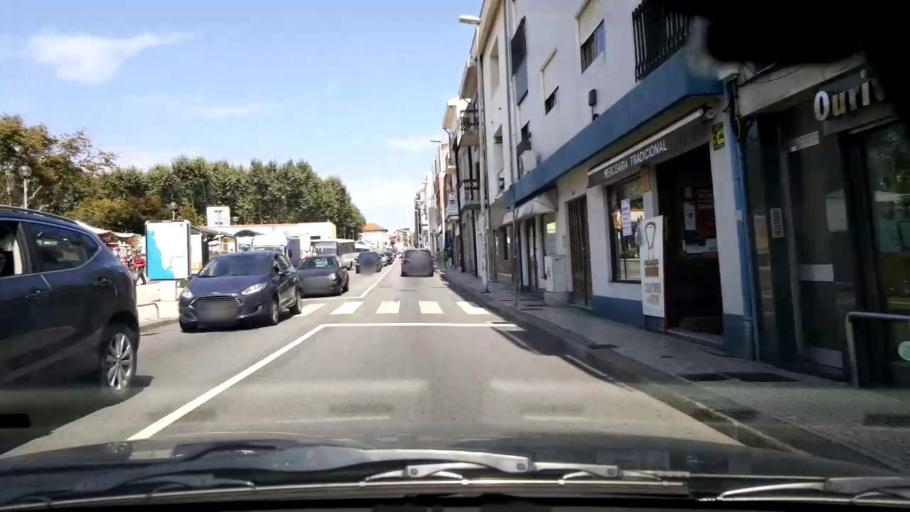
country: PT
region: Porto
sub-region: Vila do Conde
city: Vila do Conde
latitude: 41.3540
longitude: -8.7411
